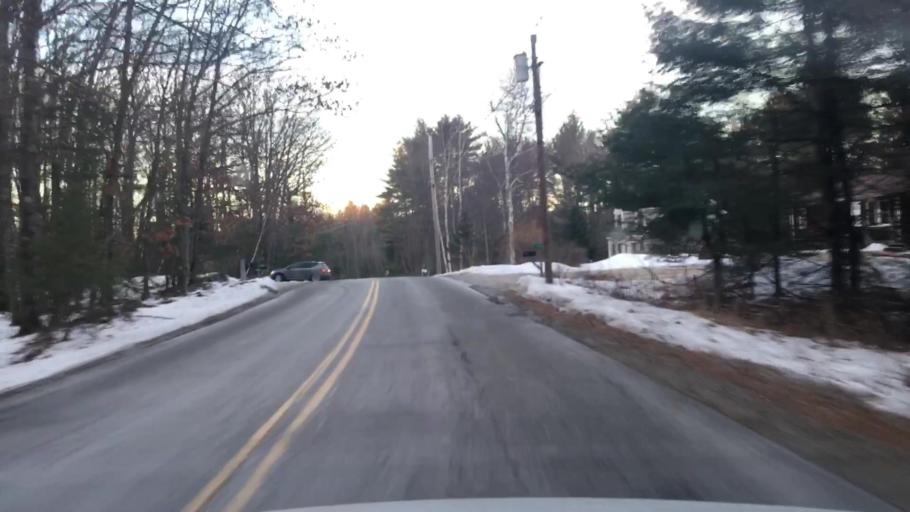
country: US
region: Maine
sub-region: York County
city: Lebanon
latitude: 43.3369
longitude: -70.8636
